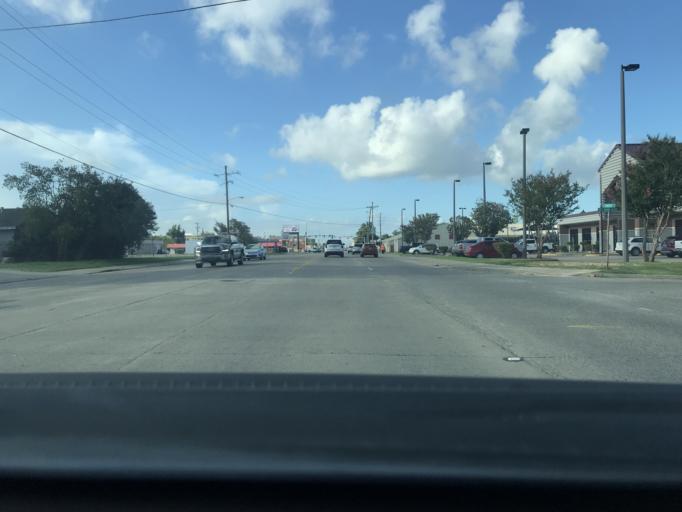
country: US
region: Louisiana
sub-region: Calcasieu Parish
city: Westlake
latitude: 30.2498
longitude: -93.2581
